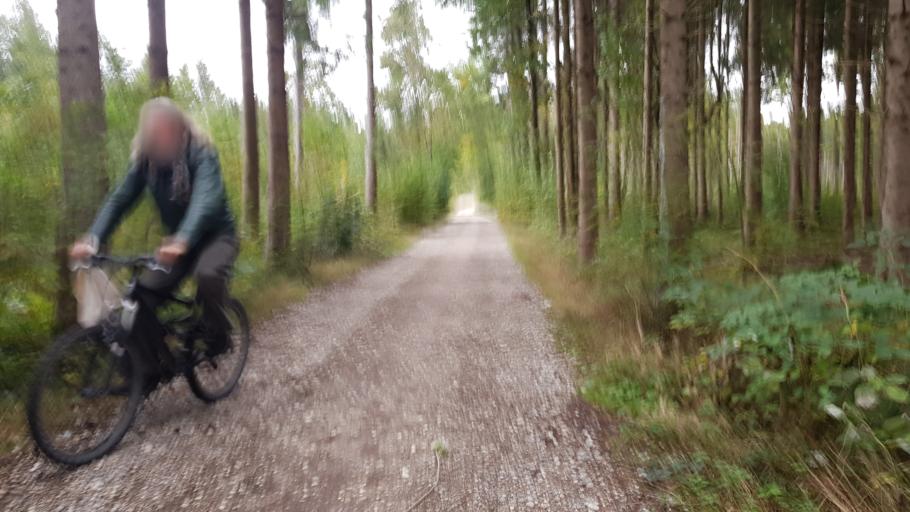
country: DE
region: Bavaria
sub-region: Upper Bavaria
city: Krailling
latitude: 48.1129
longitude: 11.3982
